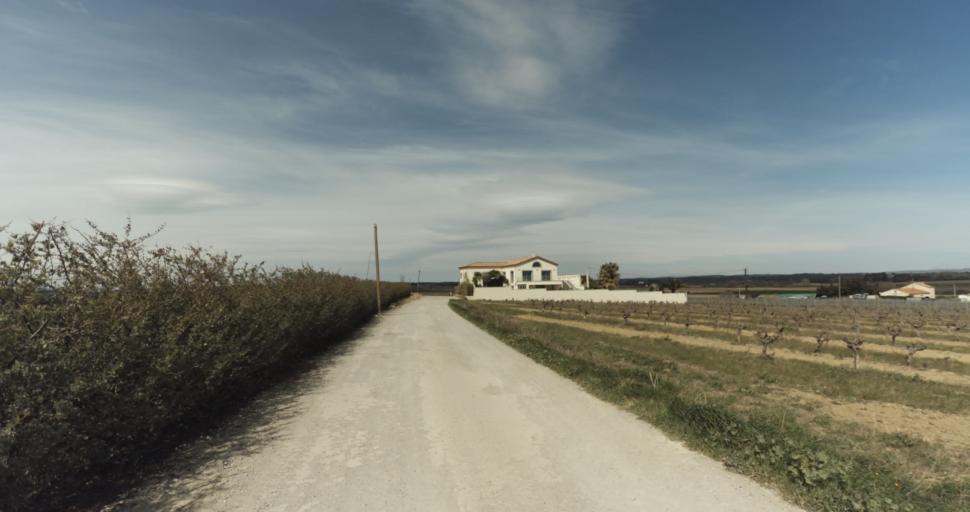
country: FR
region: Languedoc-Roussillon
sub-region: Departement de l'Herault
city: Pinet
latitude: 43.4058
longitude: 3.5505
